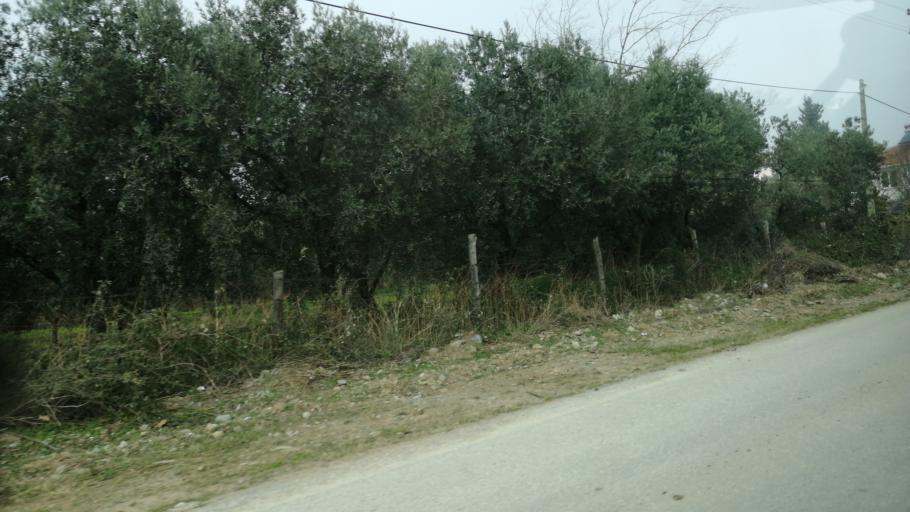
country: TR
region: Yalova
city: Cinarcik
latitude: 40.6360
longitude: 29.0785
